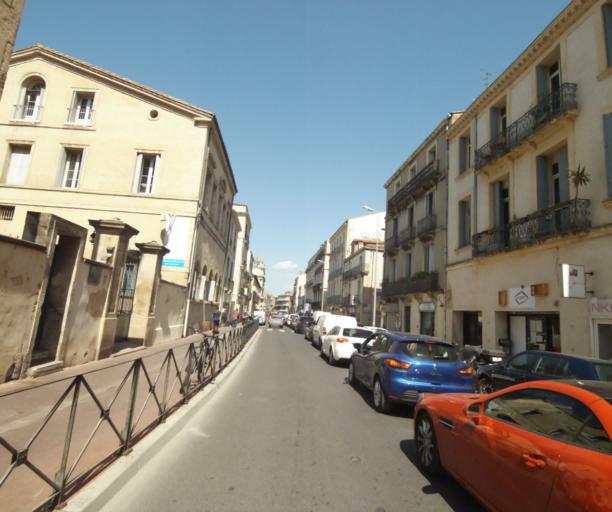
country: FR
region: Languedoc-Roussillon
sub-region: Departement de l'Herault
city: Montpellier
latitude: 43.6040
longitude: 3.8730
